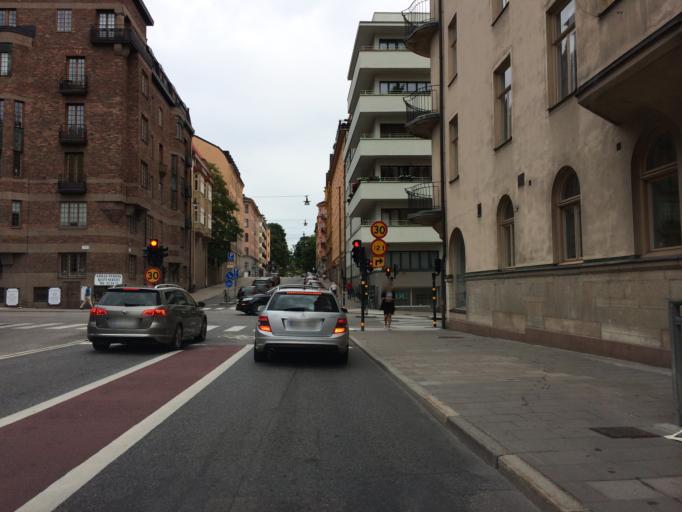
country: SE
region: Stockholm
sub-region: Stockholms Kommun
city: Stockholm
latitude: 59.3369
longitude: 18.0498
